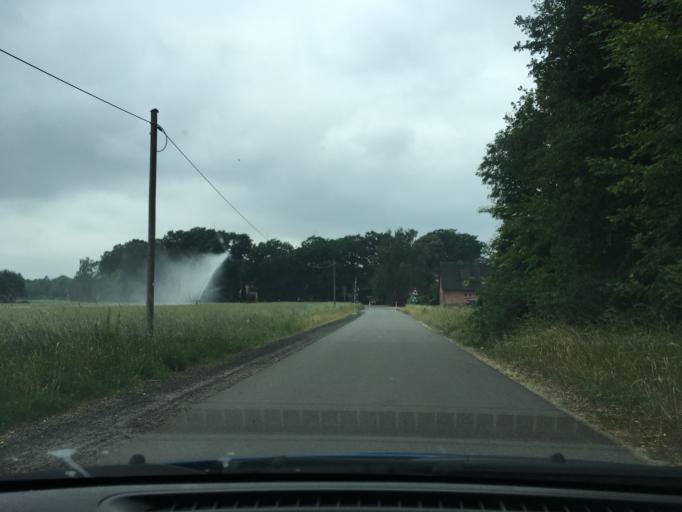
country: DE
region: Lower Saxony
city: Zernien
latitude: 53.0929
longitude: 10.8869
